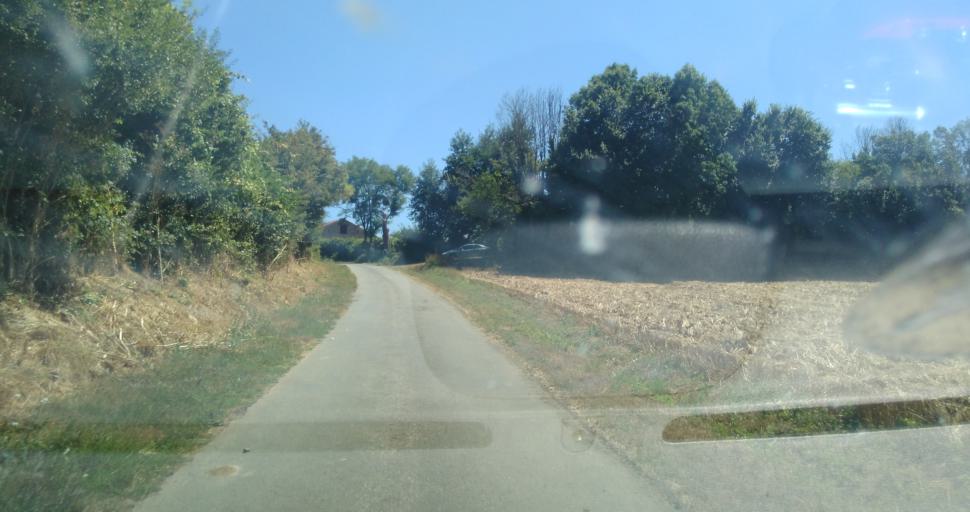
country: FR
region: Pays de la Loire
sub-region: Departement de la Vendee
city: Sainte-Hermine
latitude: 46.5771
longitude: -1.0313
